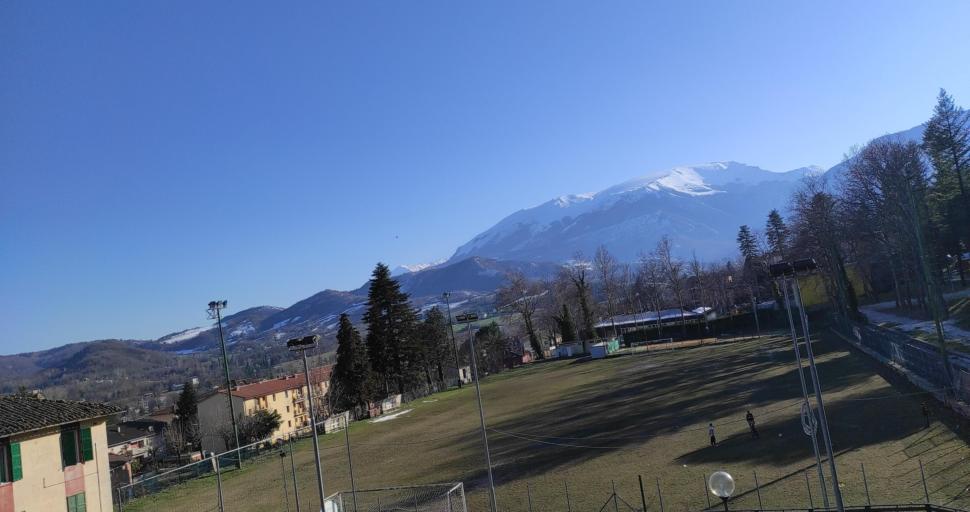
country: IT
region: The Marches
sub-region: Provincia di Macerata
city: Sarnano
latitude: 43.0351
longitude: 13.2984
